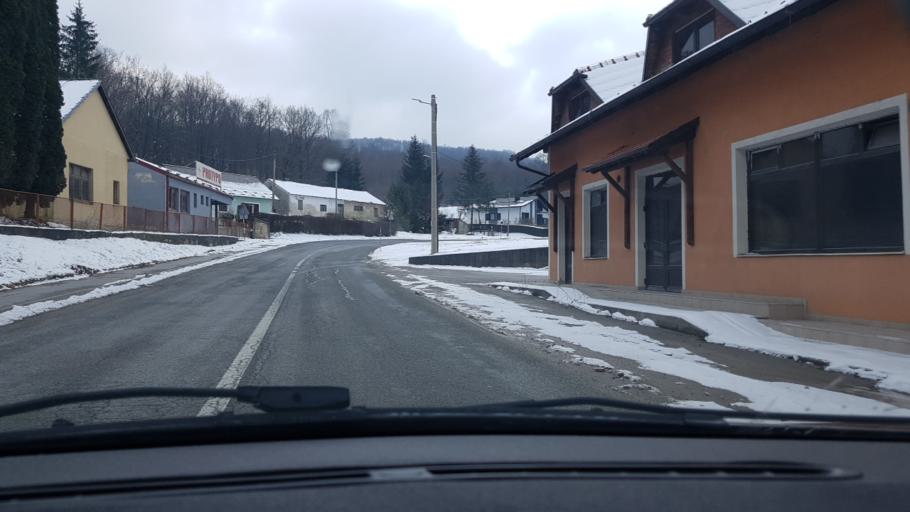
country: HR
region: Krapinsko-Zagorska
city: Mihovljan
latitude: 46.1707
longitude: 15.9800
